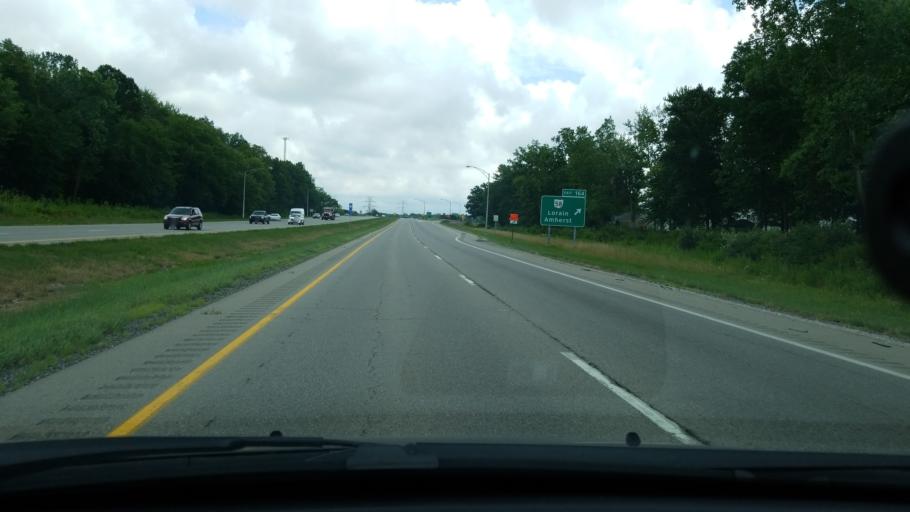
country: US
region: Ohio
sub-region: Lorain County
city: Amherst
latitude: 41.4133
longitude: -82.2167
